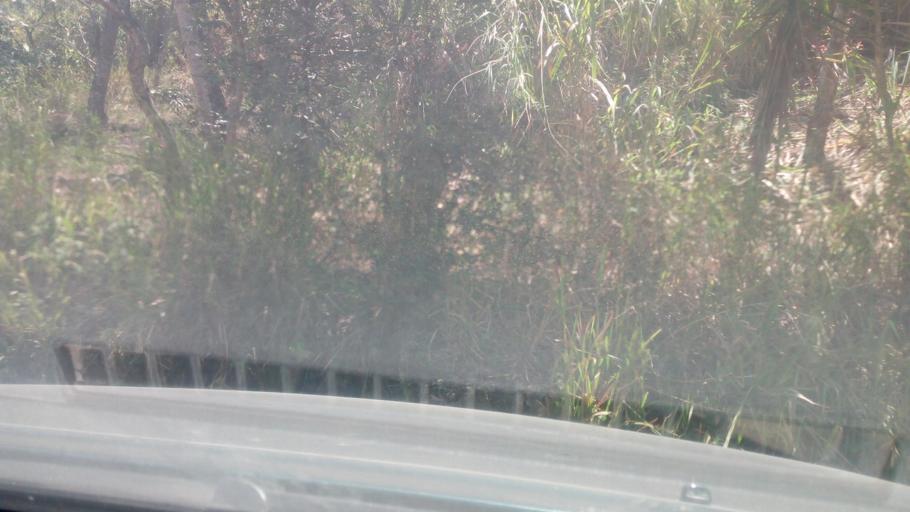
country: CO
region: Boyaca
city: Guateque
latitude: 4.9860
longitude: -73.4608
